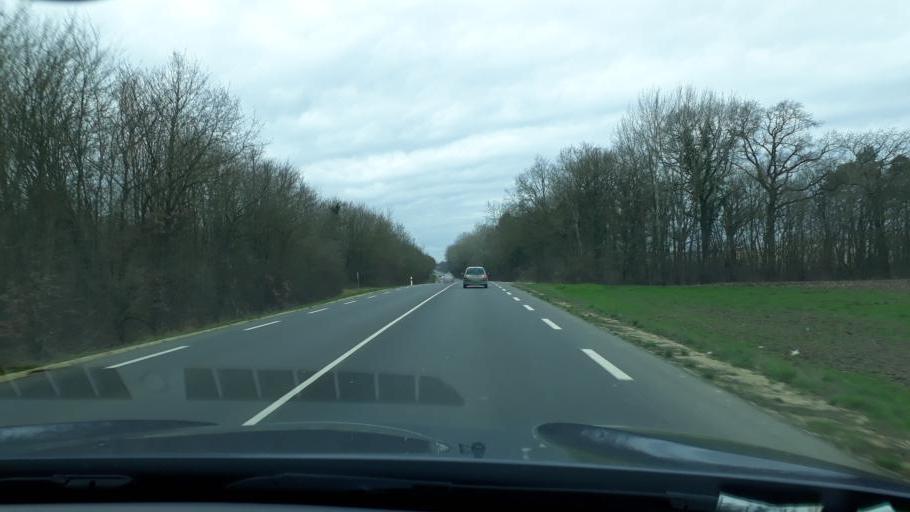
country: FR
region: Centre
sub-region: Departement du Loiret
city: Chanteau
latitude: 48.0153
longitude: 1.9595
